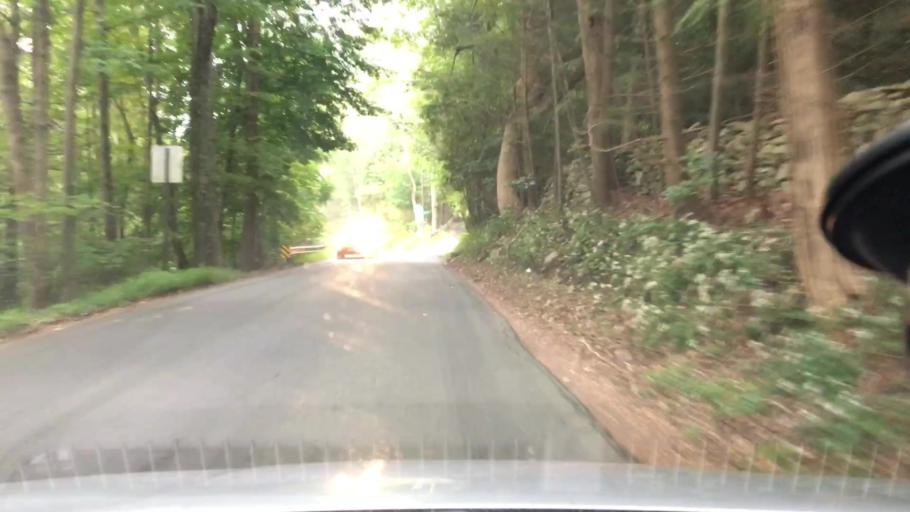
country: US
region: Pennsylvania
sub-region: Monroe County
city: Mountainhome
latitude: 41.1643
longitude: -75.2680
